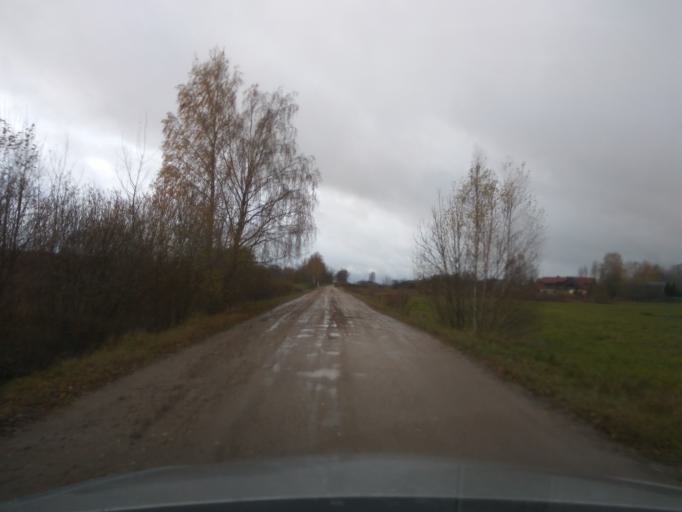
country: LV
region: Kuldigas Rajons
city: Kuldiga
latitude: 56.9689
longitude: 21.9416
